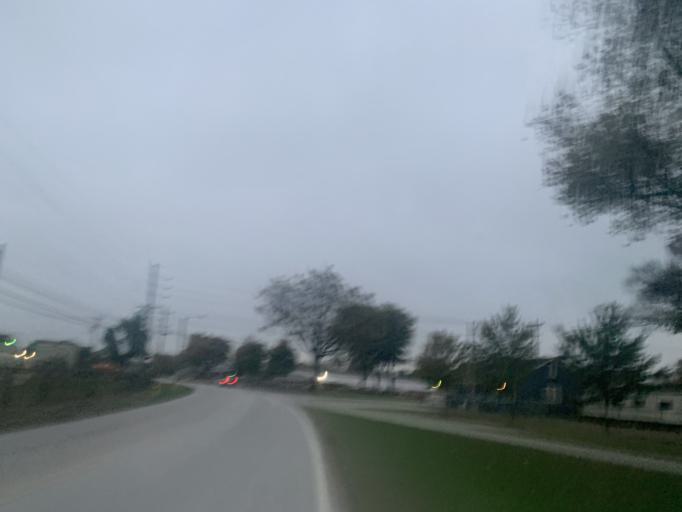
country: US
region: Kentucky
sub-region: Jefferson County
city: Shively
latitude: 38.2157
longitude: -85.8073
